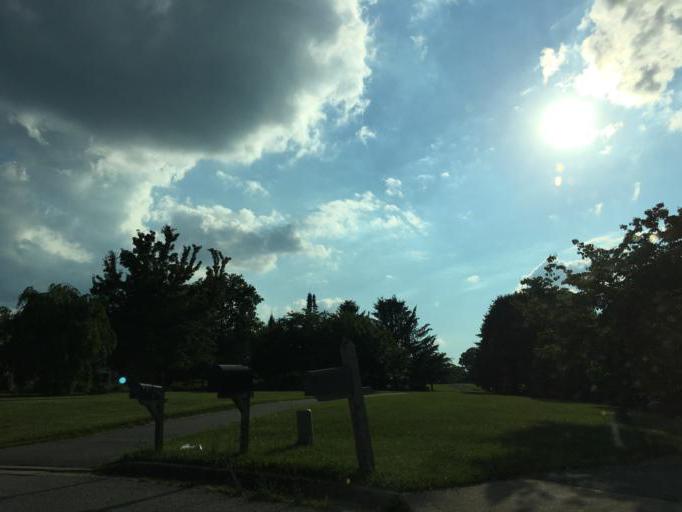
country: US
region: Maryland
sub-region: Harford County
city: Jarrettsville
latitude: 39.5187
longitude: -76.5063
